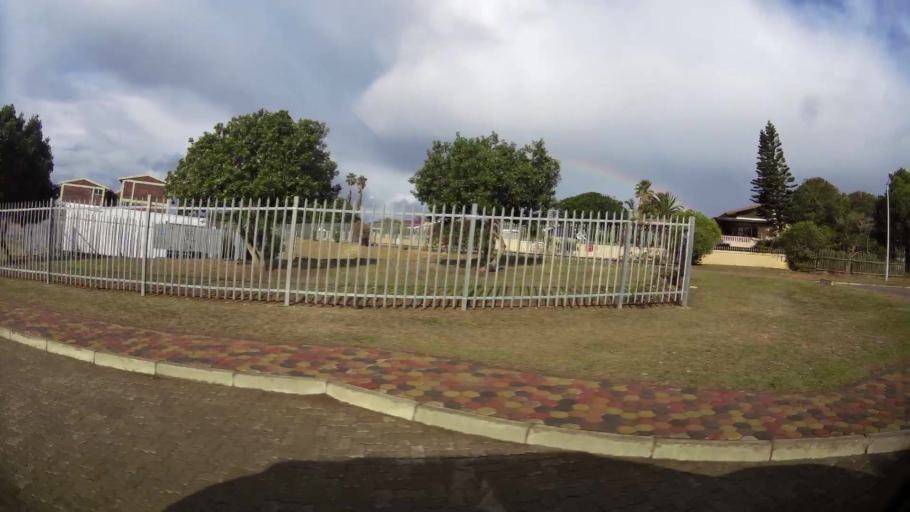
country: ZA
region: Western Cape
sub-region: Eden District Municipality
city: Mossel Bay
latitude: -34.1893
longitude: 22.1396
